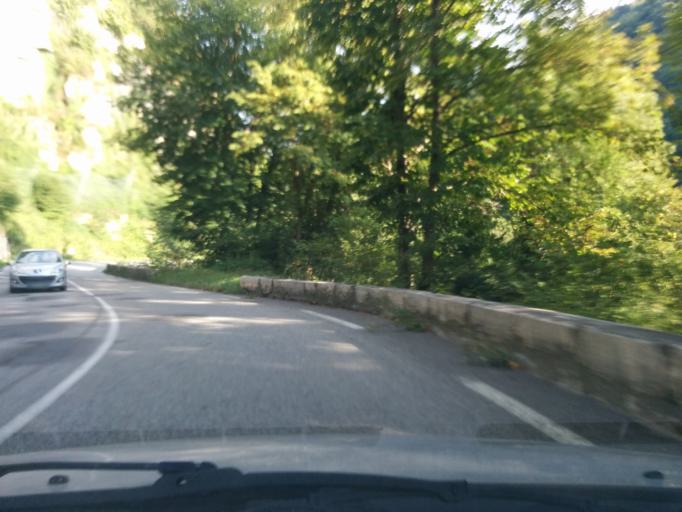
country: FR
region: Rhone-Alpes
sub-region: Departement de la Savoie
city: Saint-Beron
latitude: 45.4825
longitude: 5.7231
